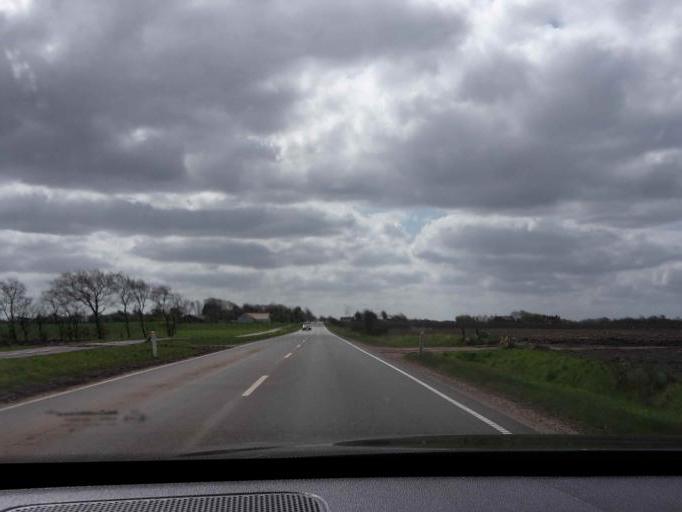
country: DK
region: South Denmark
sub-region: Varde Kommune
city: Olgod
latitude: 55.7543
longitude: 8.6200
